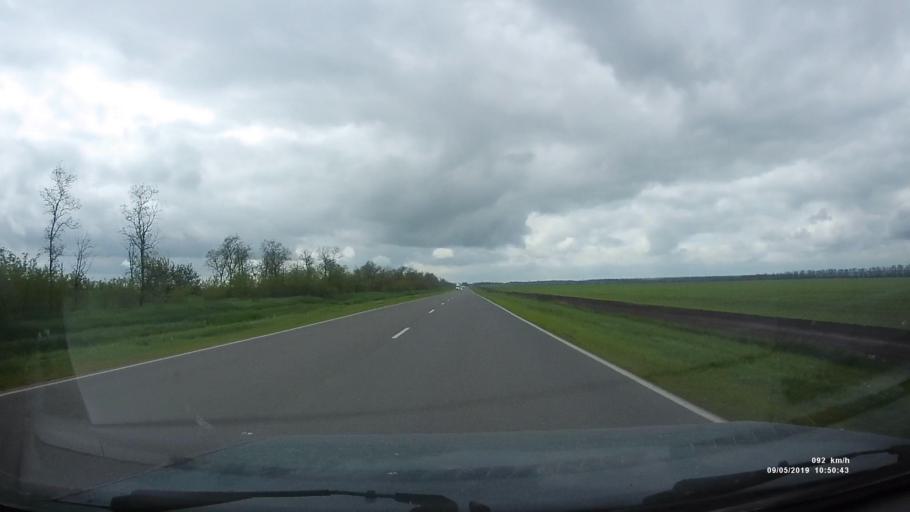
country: RU
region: Rostov
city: Peshkovo
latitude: 46.9248
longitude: 39.3557
